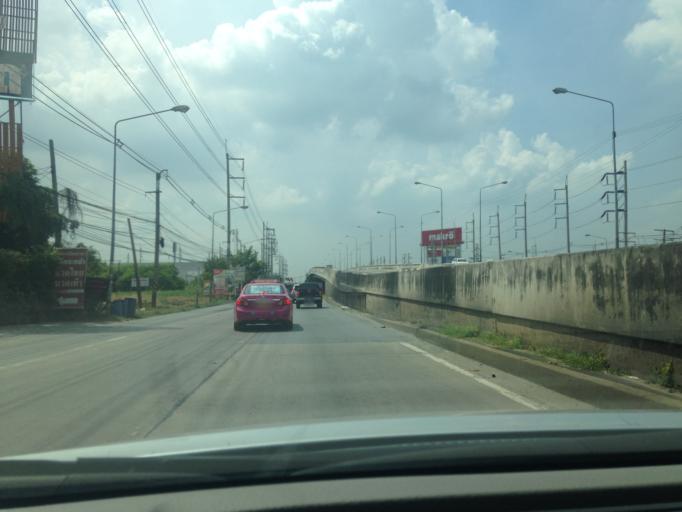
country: TH
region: Pathum Thani
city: Pathum Thani
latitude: 14.0299
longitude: 100.5285
